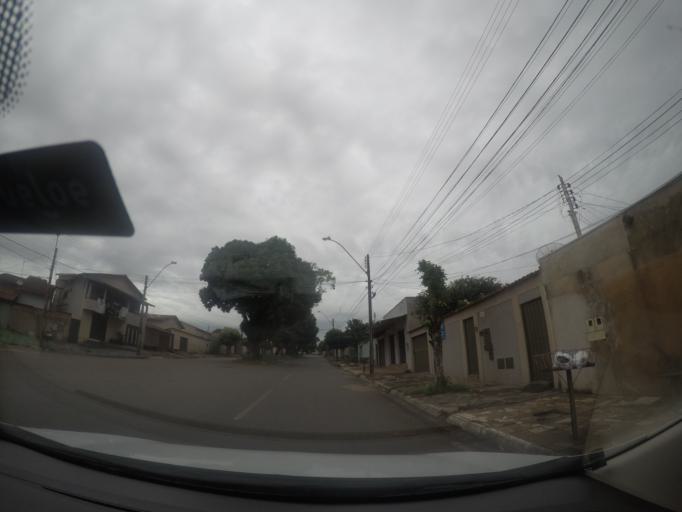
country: BR
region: Goias
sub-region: Goiania
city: Goiania
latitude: -16.6168
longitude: -49.3014
